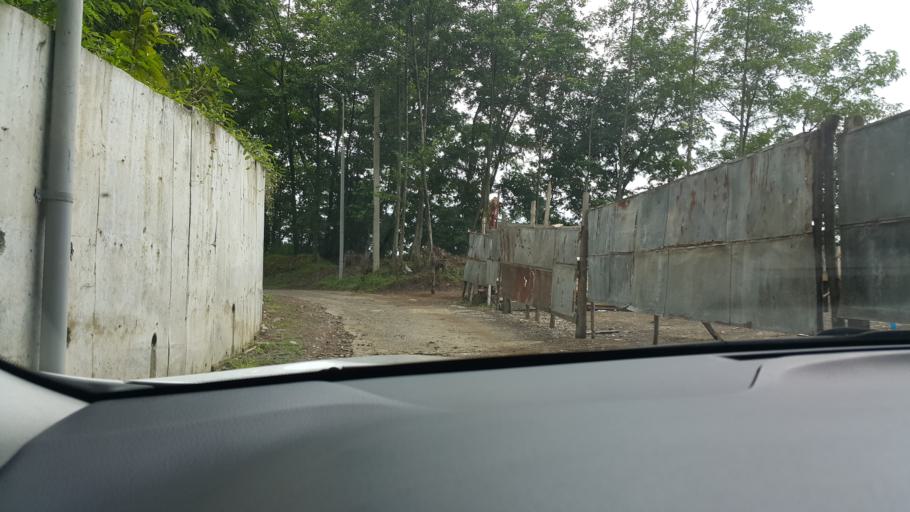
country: GE
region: Ajaria
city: Khelvachauri
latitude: 41.6156
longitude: 41.6567
